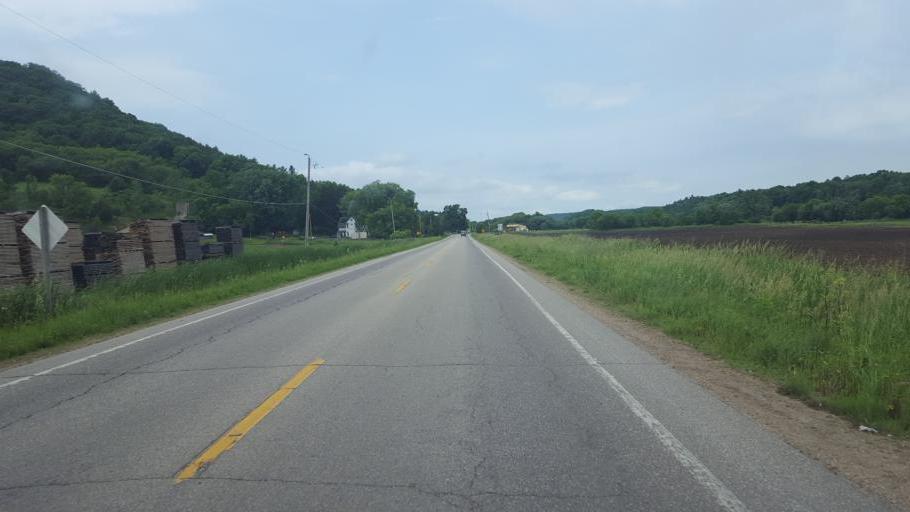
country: US
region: Wisconsin
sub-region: Monroe County
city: Cashton
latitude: 43.7233
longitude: -90.5977
